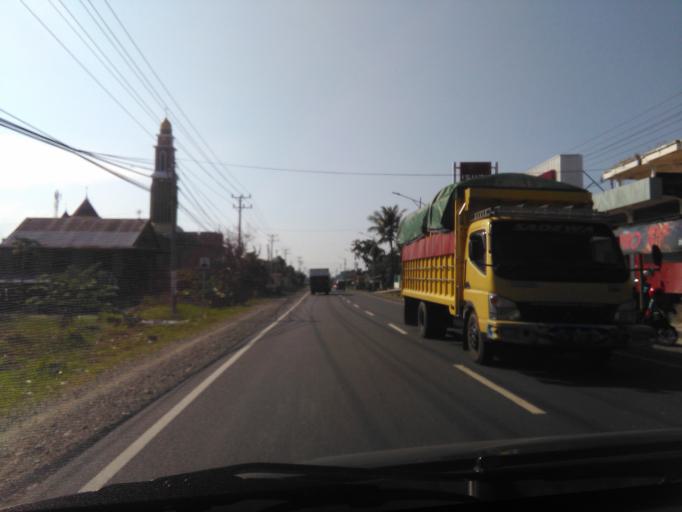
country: ID
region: South Sulawesi
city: Uluale
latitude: -3.9120
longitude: 119.7612
